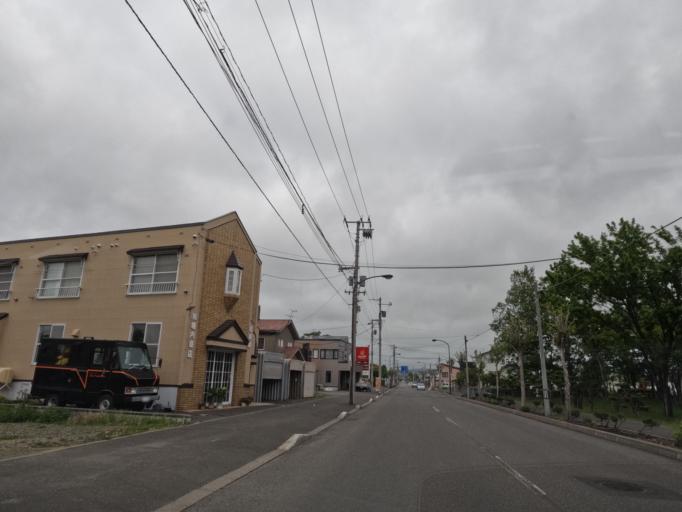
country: JP
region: Hokkaido
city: Tobetsu
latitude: 43.2236
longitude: 141.5181
